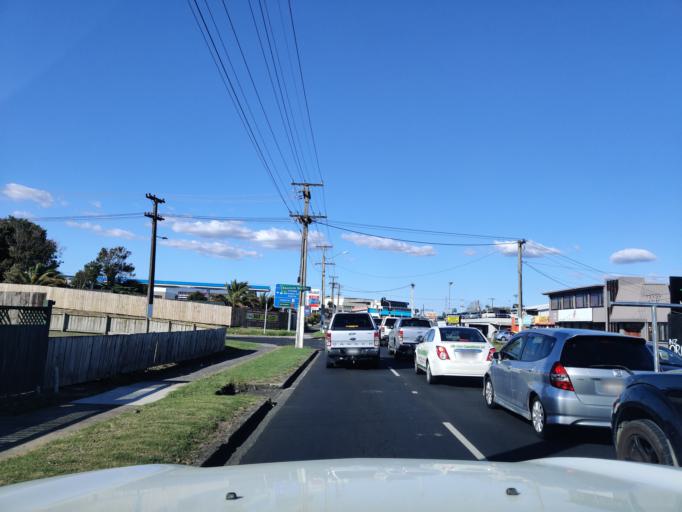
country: NZ
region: Auckland
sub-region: Auckland
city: Takanini
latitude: -37.0332
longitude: 174.9043
